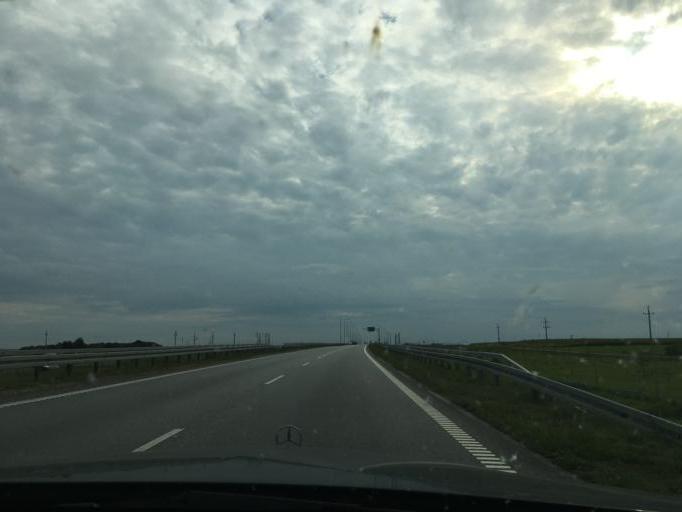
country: PL
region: Podlasie
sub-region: Powiat kolnenski
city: Stawiski
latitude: 53.3967
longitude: 22.1543
